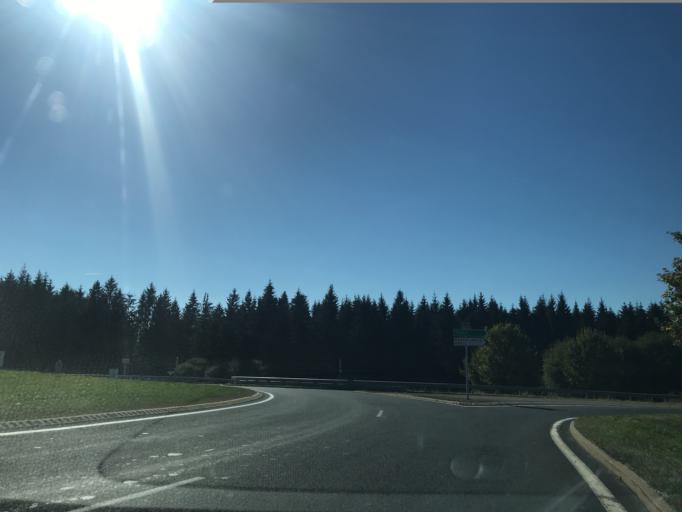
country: FR
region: Auvergne
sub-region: Departement du Puy-de-Dome
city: Saint-Sauves-d'Auvergne
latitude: 45.6559
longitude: 2.6894
